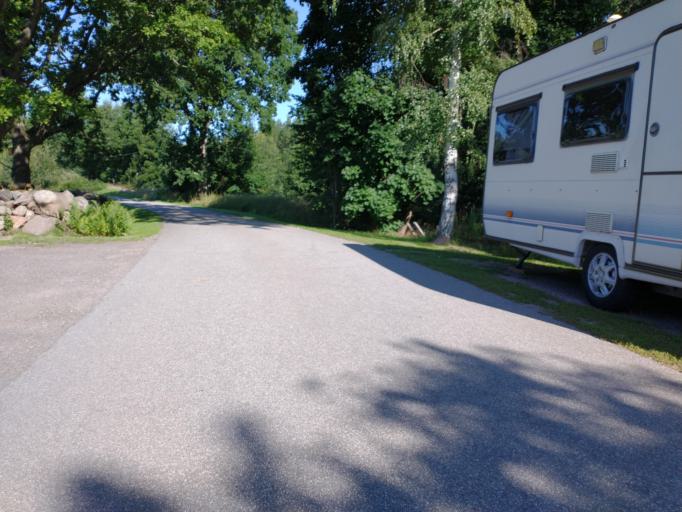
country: SE
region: Kalmar
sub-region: Kalmar Kommun
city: Lindsdal
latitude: 56.7853
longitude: 16.2678
